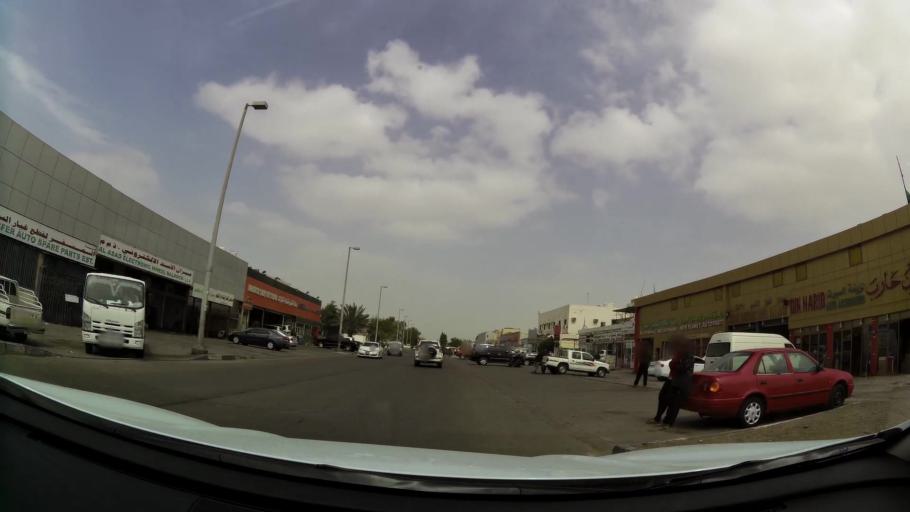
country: AE
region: Abu Dhabi
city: Abu Dhabi
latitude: 24.3784
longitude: 54.5147
